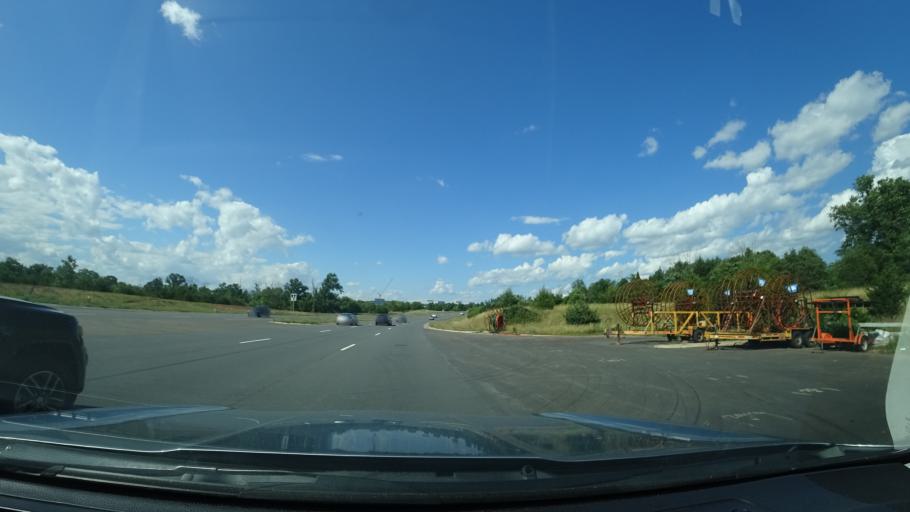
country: US
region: Virginia
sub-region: Loudoun County
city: Ashburn
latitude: 39.0048
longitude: -77.4739
